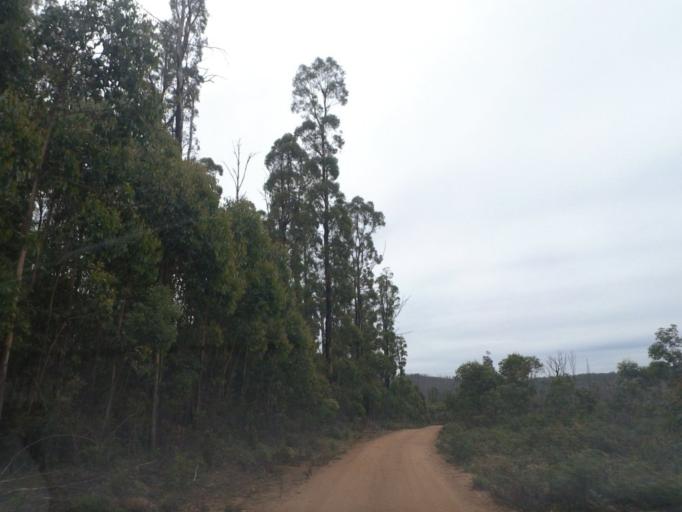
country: AU
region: Victoria
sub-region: Murrindindi
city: Alexandra
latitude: -37.3972
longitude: 145.5891
